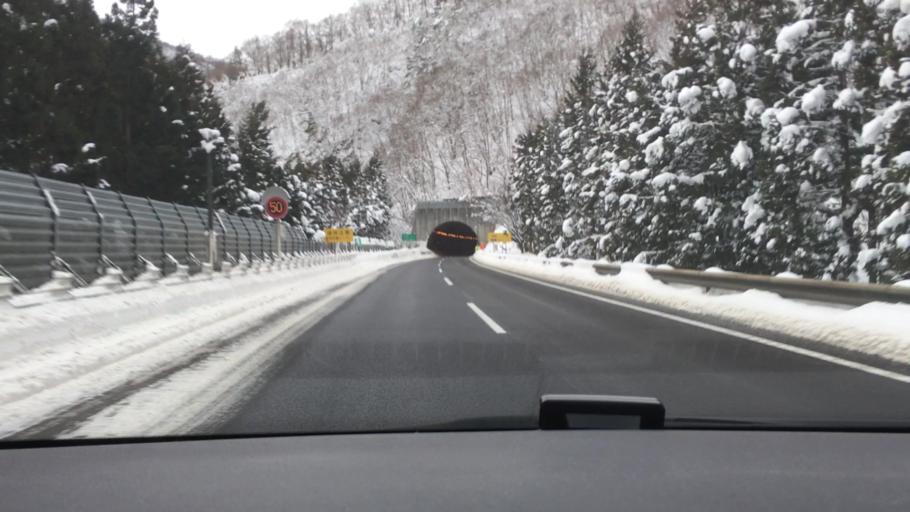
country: JP
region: Akita
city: Hanawa
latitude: 40.1160
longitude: 140.8911
